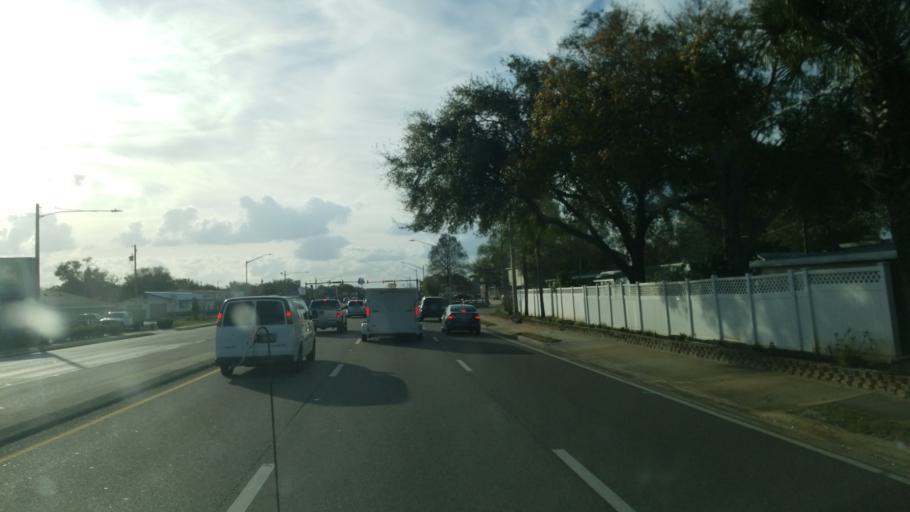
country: US
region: Florida
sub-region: Osceola County
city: Saint Cloud
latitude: 28.2460
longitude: -81.2701
